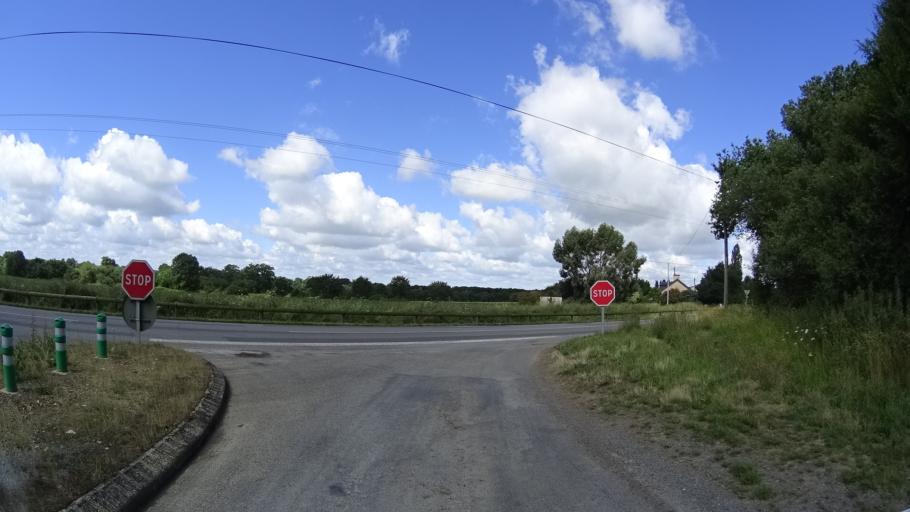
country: FR
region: Brittany
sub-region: Departement d'Ille-et-Vilaine
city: Le Rheu
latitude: 48.1109
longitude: -1.8051
